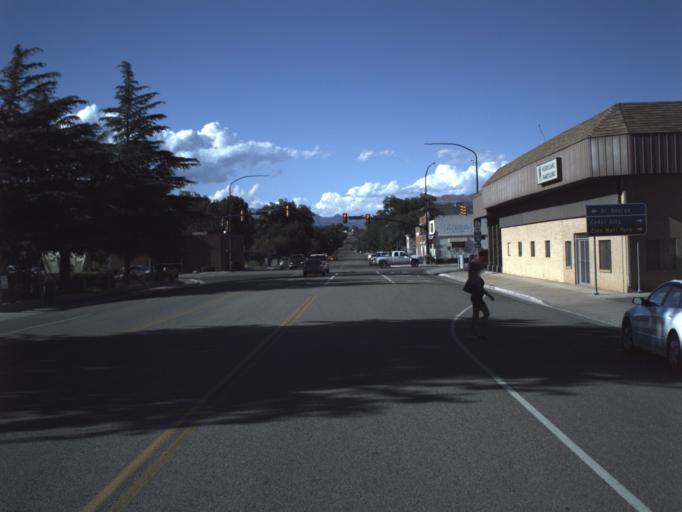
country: US
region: Utah
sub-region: Washington County
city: Hurricane
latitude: 37.1756
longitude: -113.2881
